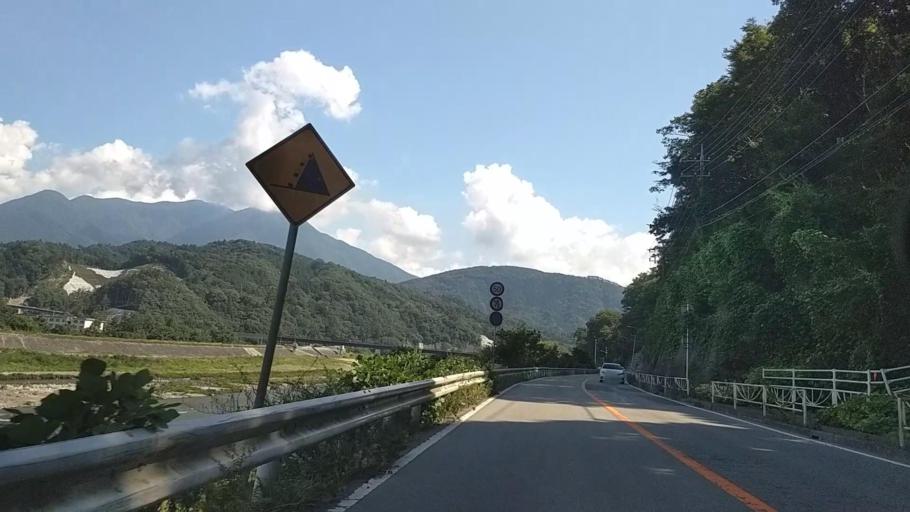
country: JP
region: Yamanashi
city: Ryuo
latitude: 35.4610
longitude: 138.4414
